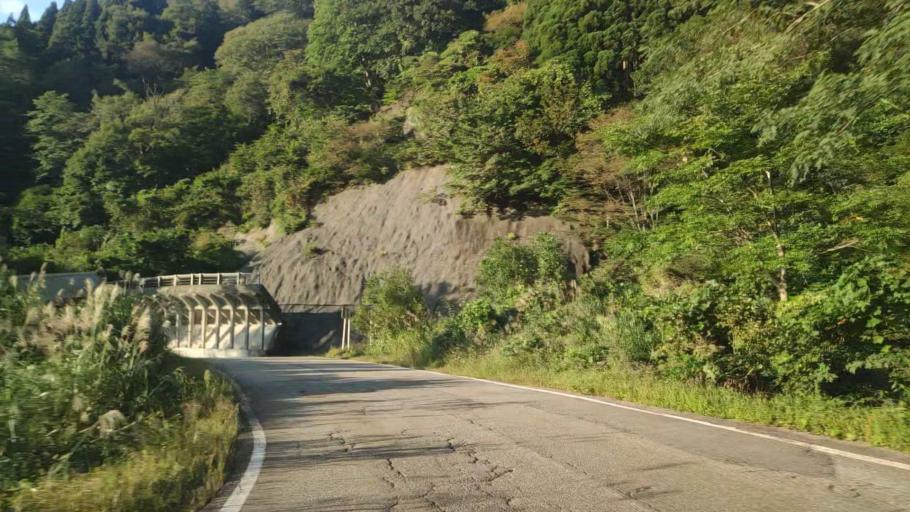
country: JP
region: Toyama
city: Yatsuomachi-higashikumisaka
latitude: 36.5184
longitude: 137.0304
